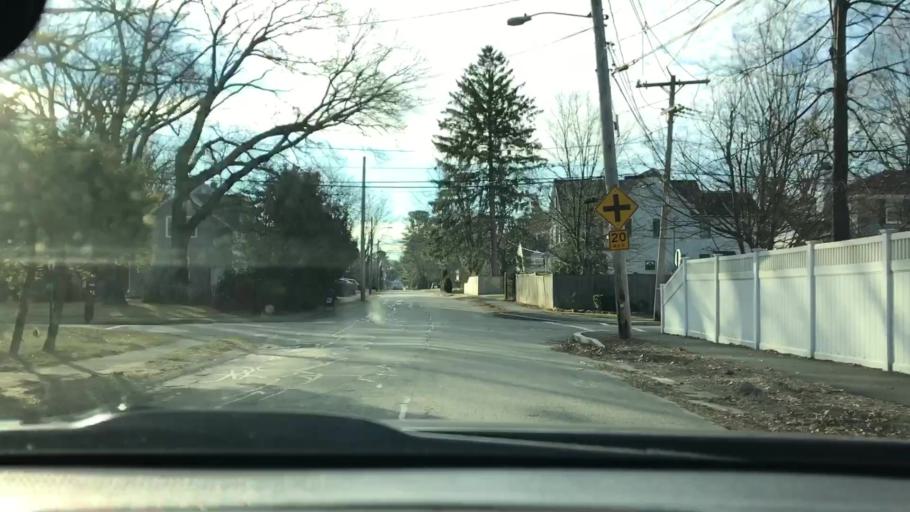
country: US
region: Massachusetts
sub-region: Norfolk County
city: Needham
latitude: 42.2921
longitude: -71.2295
